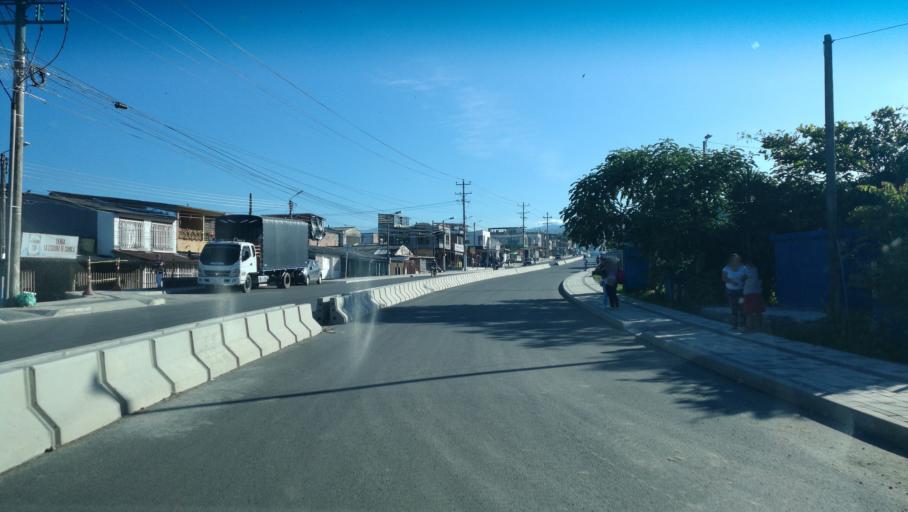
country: CO
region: Quindio
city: Armenia
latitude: 4.5184
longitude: -75.7120
